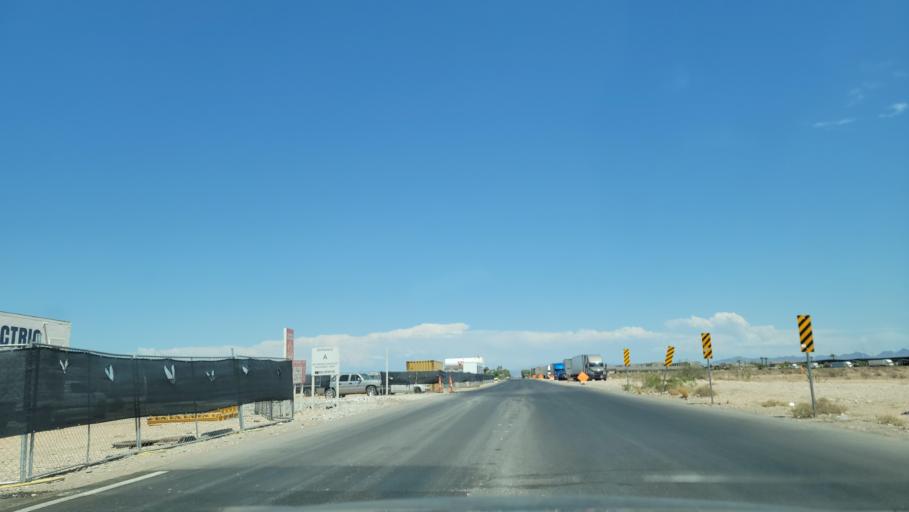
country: US
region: Nevada
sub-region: Clark County
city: Enterprise
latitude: 36.0611
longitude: -115.2769
